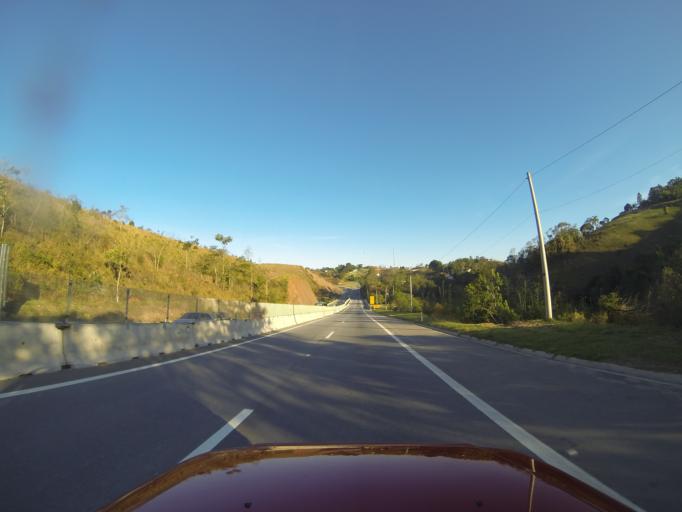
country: BR
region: Sao Paulo
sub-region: Santa Branca
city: Santa Branca
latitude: -23.3077
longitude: -45.7669
